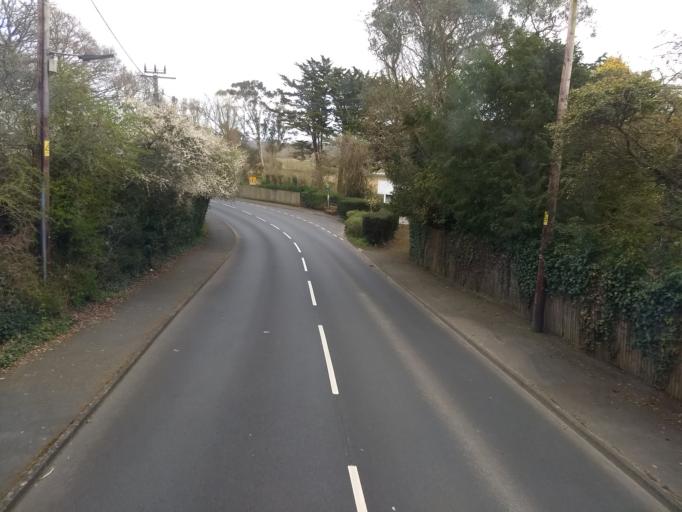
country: GB
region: England
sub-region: Isle of Wight
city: Seaview
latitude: 50.6939
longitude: -1.1125
